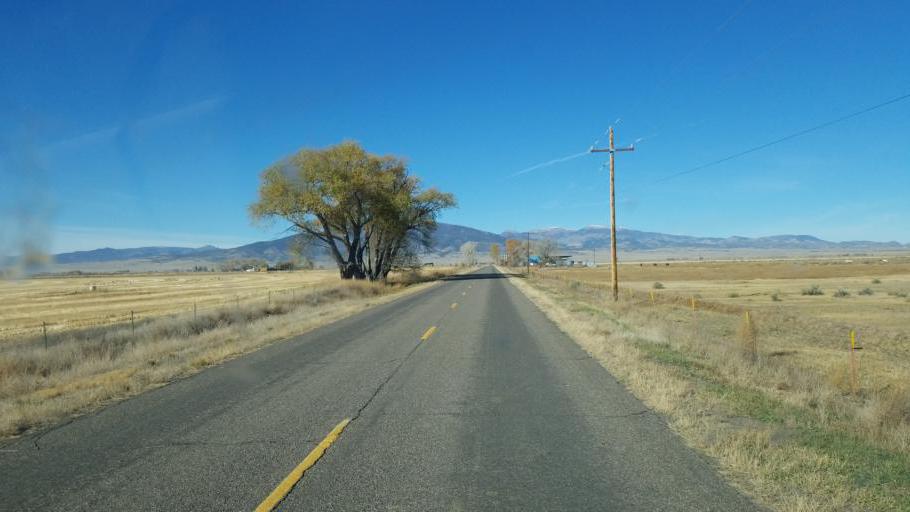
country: US
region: Colorado
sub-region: Rio Grande County
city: Monte Vista
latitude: 37.4591
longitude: -106.0790
